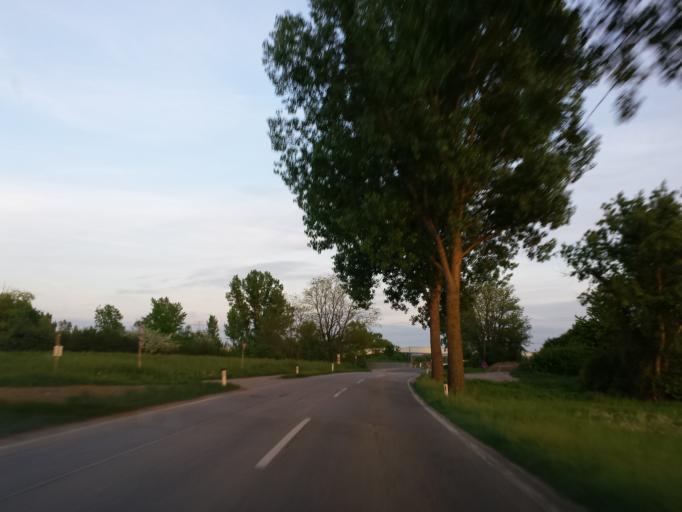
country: AT
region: Lower Austria
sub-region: Politischer Bezirk Tulln
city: Michelhausen
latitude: 48.3369
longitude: 15.9391
